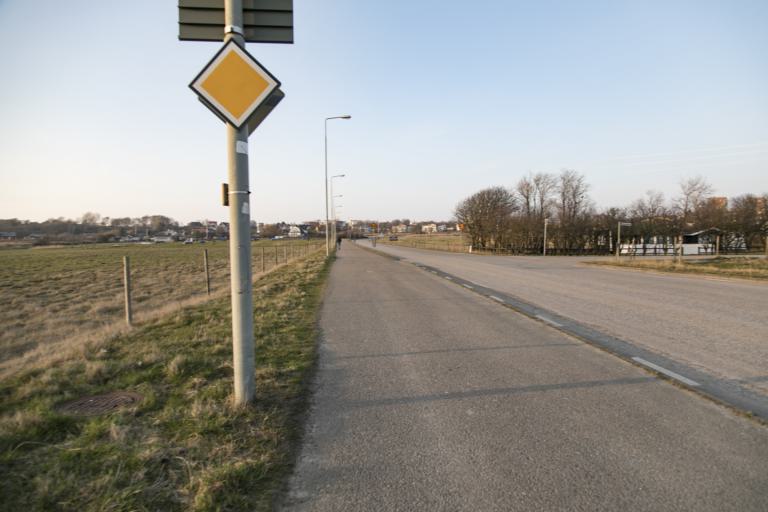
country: SE
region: Halland
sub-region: Varbergs Kommun
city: Varberg
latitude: 57.0862
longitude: 12.2534
